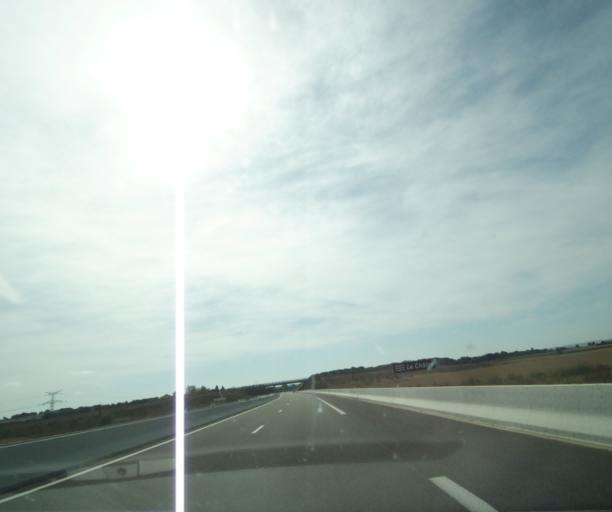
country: FR
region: Auvergne
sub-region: Departement de l'Allier
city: Vendat
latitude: 46.1301
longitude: 3.3002
